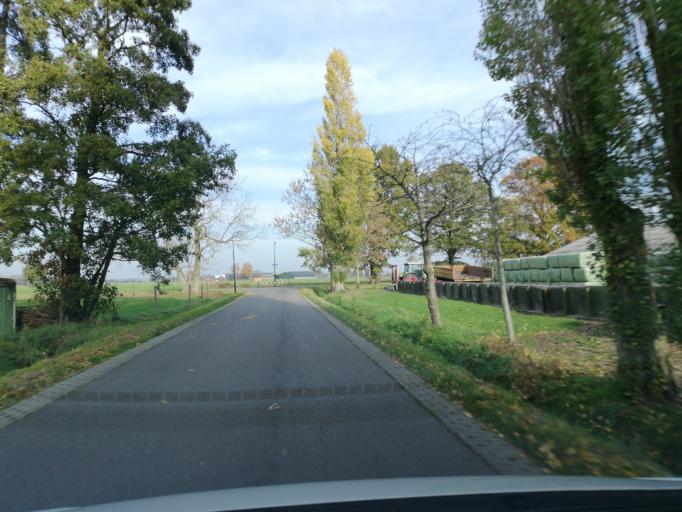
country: NL
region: Gelderland
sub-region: Gemeente Epe
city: Vaassen
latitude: 52.2552
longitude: 6.0169
